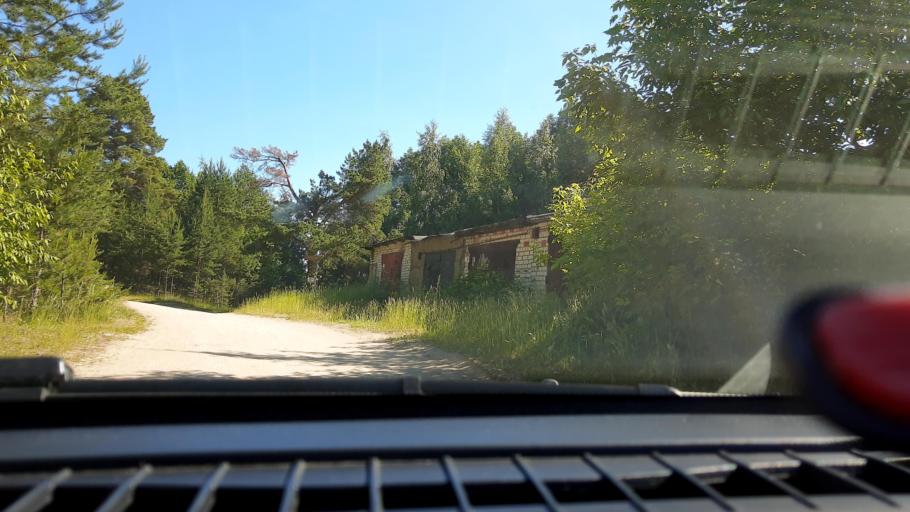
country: RU
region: Nizjnij Novgorod
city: Gidrotorf
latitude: 56.5053
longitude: 43.5381
